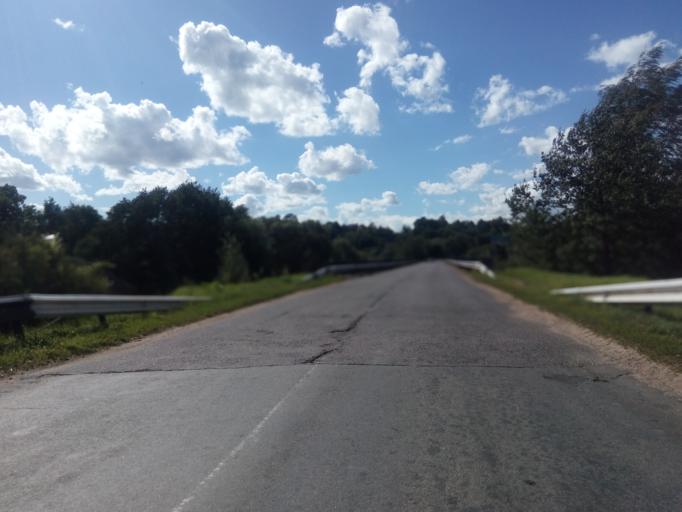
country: BY
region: Vitebsk
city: Dzisna
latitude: 55.7018
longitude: 28.1894
